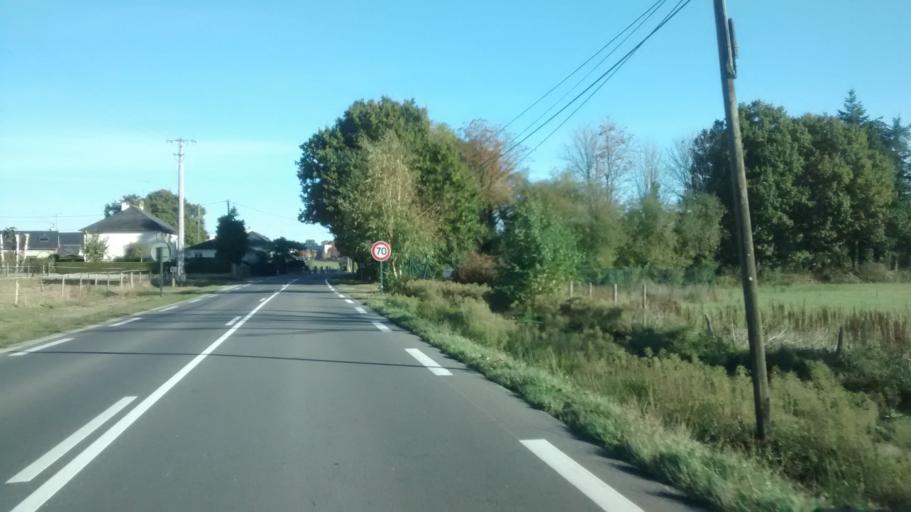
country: FR
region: Brittany
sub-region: Departement d'Ille-et-Vilaine
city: Vitre
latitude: 48.1051
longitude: -1.2213
